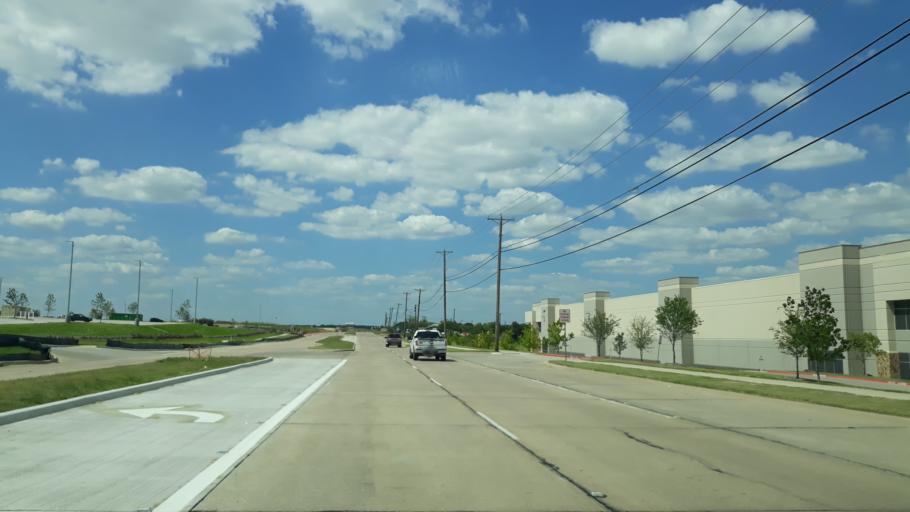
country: US
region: Texas
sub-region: Tarrant County
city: Euless
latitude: 32.8430
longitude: -97.0217
